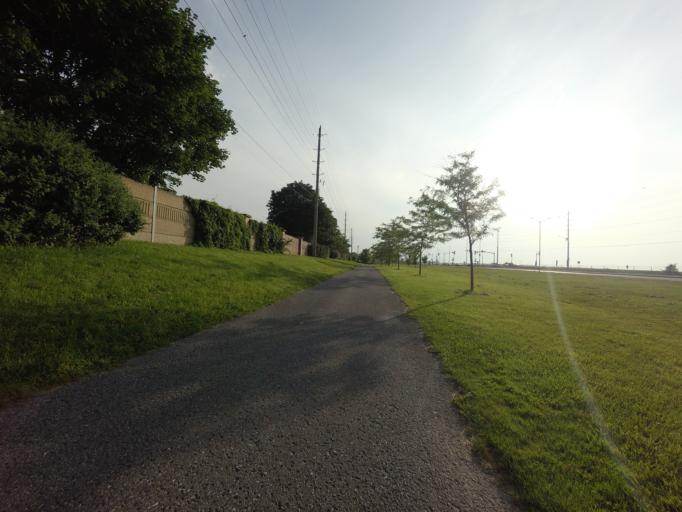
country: CA
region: Ontario
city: Bells Corners
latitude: 45.2959
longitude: -75.7376
